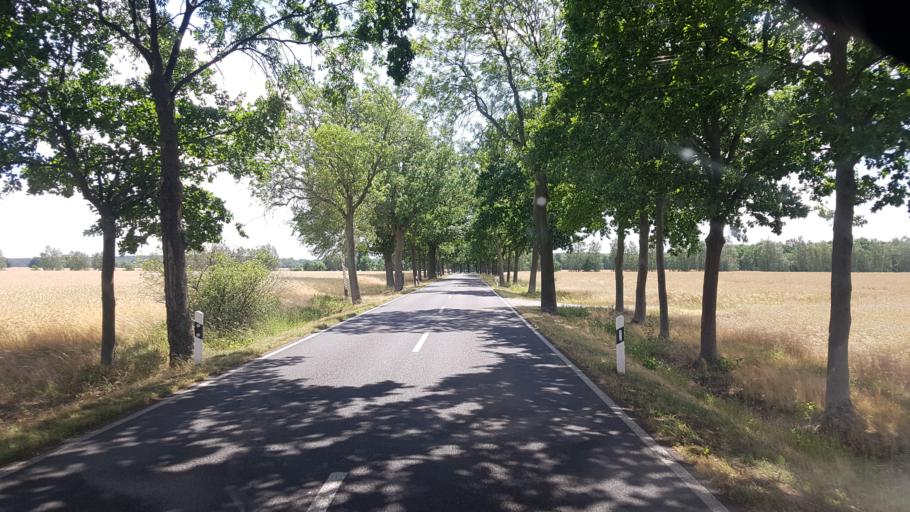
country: DE
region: Brandenburg
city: Sallgast
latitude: 51.6033
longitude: 13.8455
